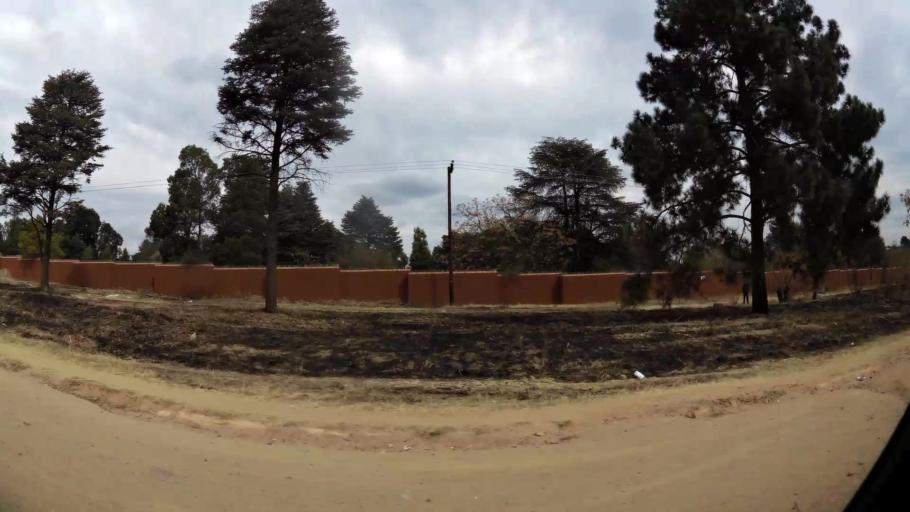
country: ZA
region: Gauteng
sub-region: West Rand District Municipality
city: Muldersdriseloop
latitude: -26.0576
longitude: 27.8985
